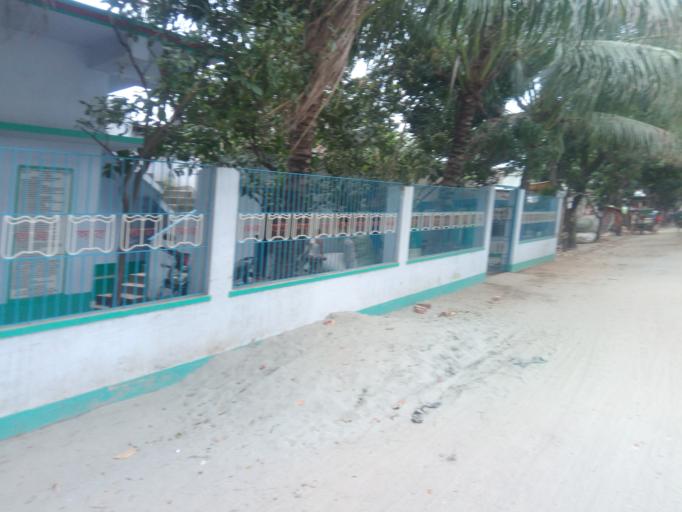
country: BD
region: Dhaka
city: Azimpur
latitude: 23.7085
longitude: 90.3774
